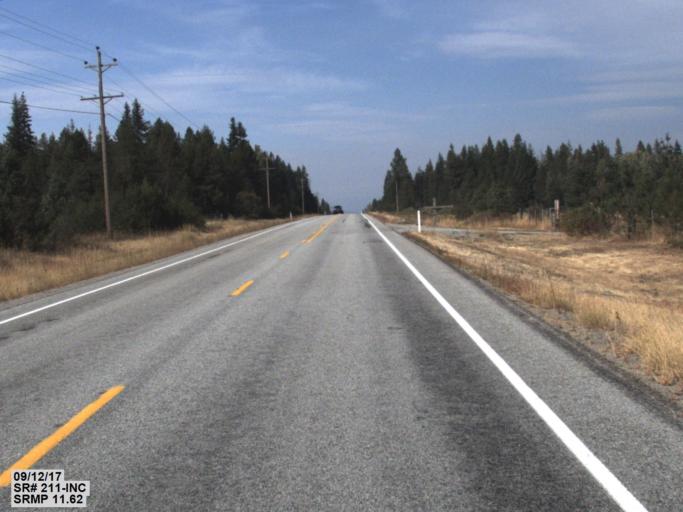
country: US
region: Washington
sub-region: Pend Oreille County
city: Newport
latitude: 48.2535
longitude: -117.2845
